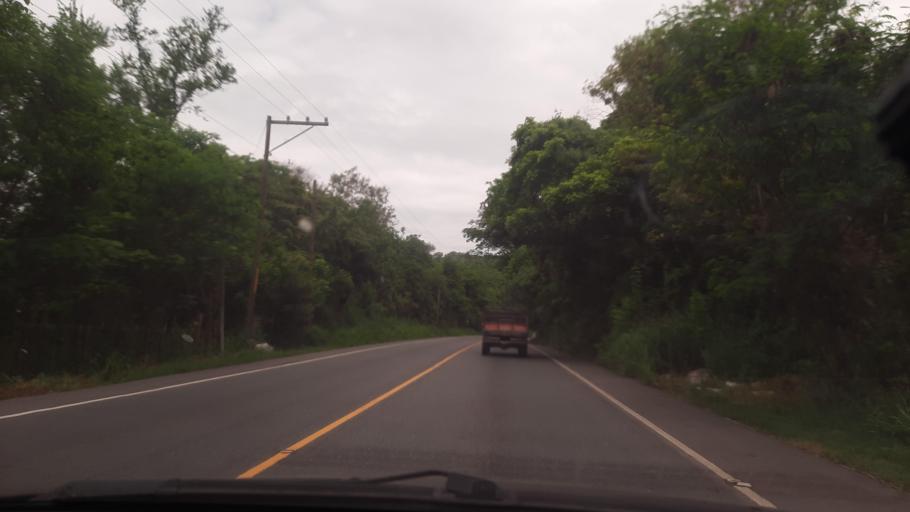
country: GT
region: Zacapa
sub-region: Municipio de Zacapa
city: Gualan
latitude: 15.1599
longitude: -89.3183
